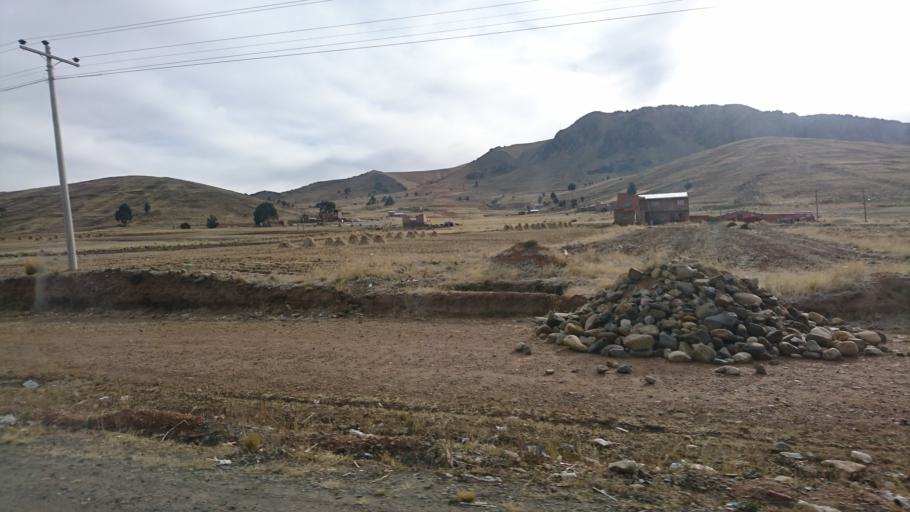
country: BO
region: La Paz
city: La Paz
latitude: -16.4146
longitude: -68.3450
